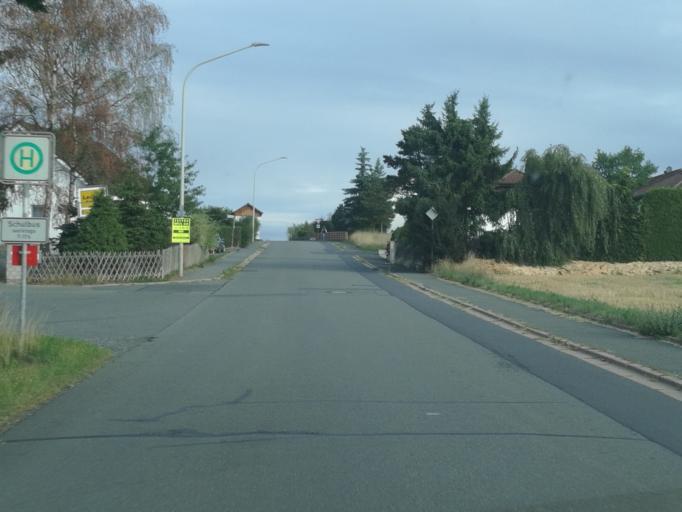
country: DE
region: Bavaria
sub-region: Upper Franconia
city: Dohlau
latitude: 50.2985
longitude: 11.9696
